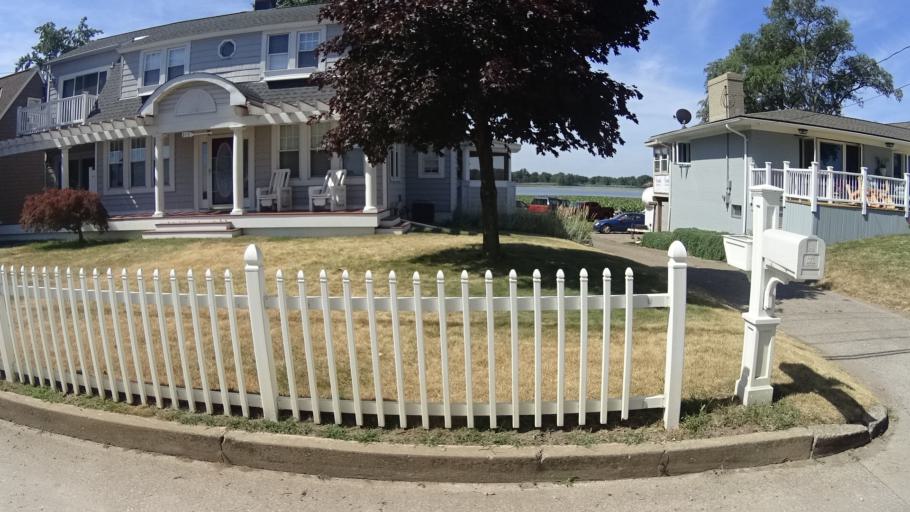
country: US
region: Ohio
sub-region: Erie County
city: Huron
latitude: 41.4357
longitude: -82.6249
